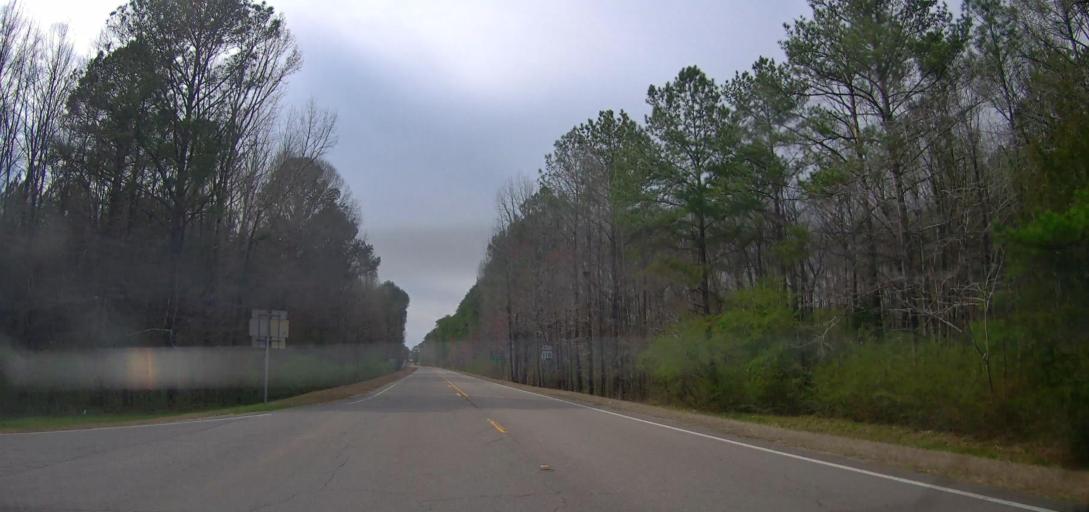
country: US
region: Alabama
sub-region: Walker County
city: Carbon Hill
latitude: 33.8760
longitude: -87.4685
